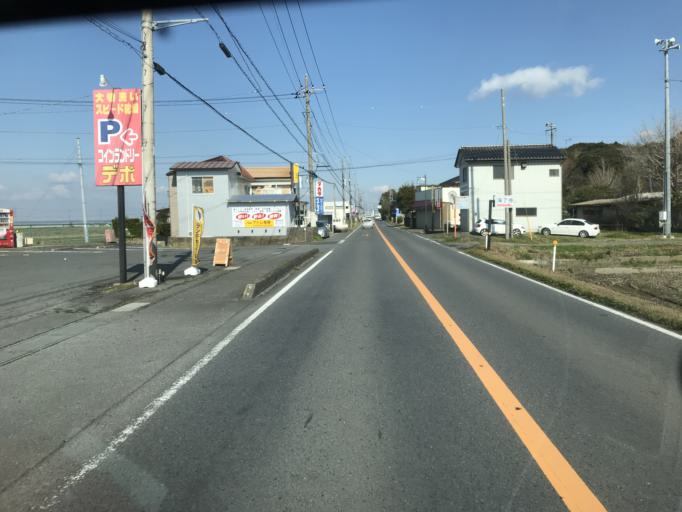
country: JP
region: Ibaraki
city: Itako
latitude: 35.9874
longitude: 140.4803
